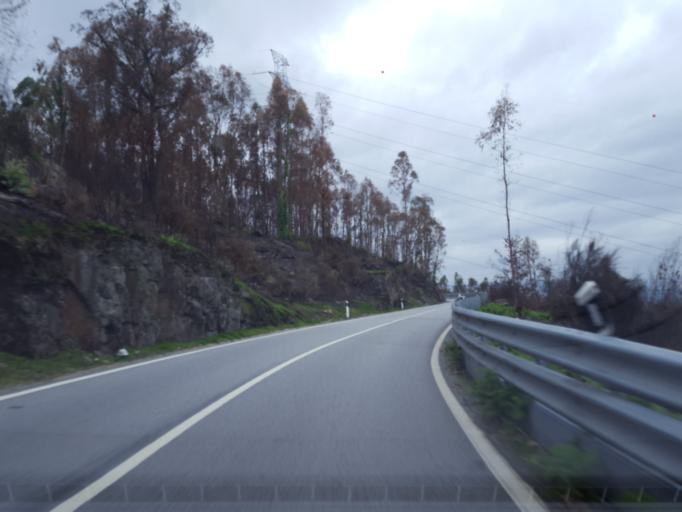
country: PT
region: Porto
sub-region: Marco de Canaveses
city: Marco de Canavezes
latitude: 41.1520
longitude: -8.1334
